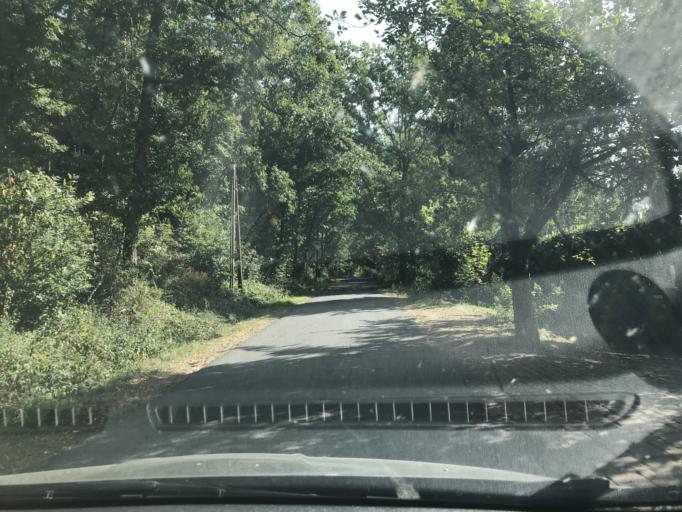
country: DE
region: Hesse
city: Hochst im Odenwald
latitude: 49.8366
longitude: 8.9801
